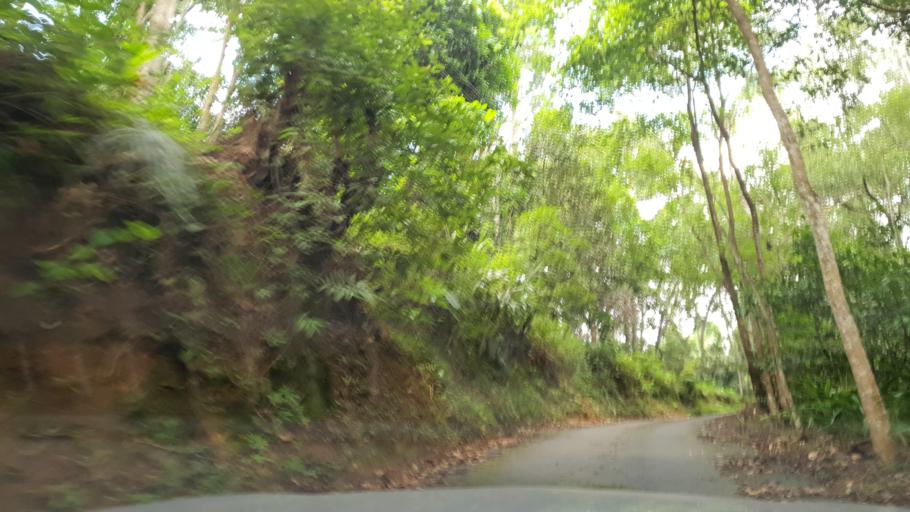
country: TH
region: Chiang Mai
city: Mae On
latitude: 18.9495
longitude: 99.3051
